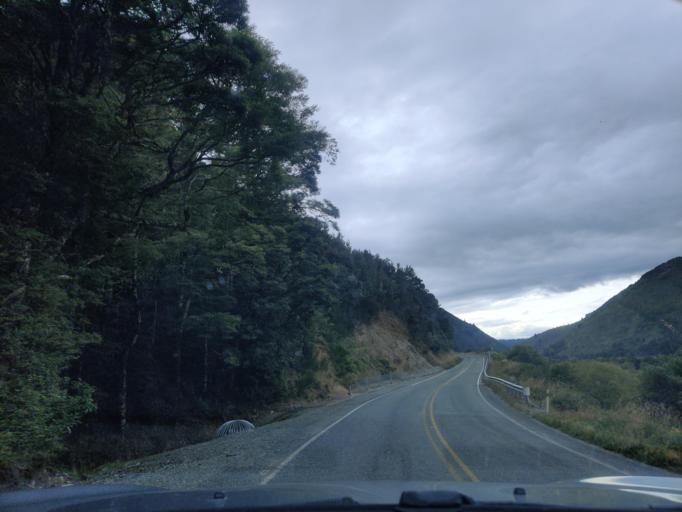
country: NZ
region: Tasman
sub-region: Tasman District
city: Wakefield
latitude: -41.6969
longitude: 172.6289
